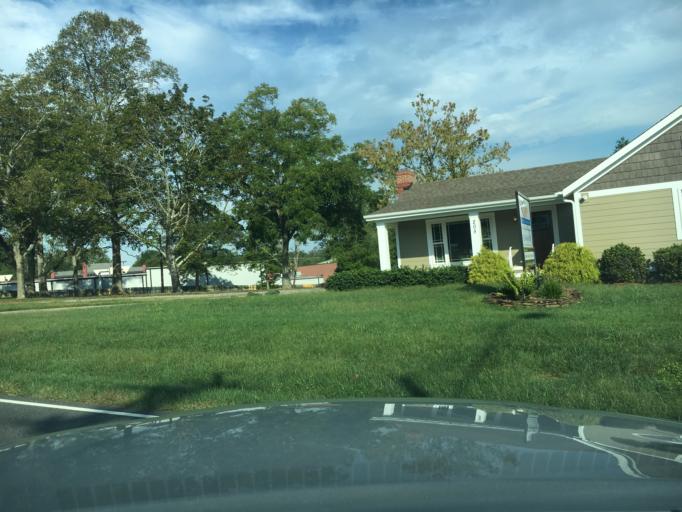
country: US
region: North Carolina
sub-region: Catawba County
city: Hickory
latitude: 35.7709
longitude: -81.3261
